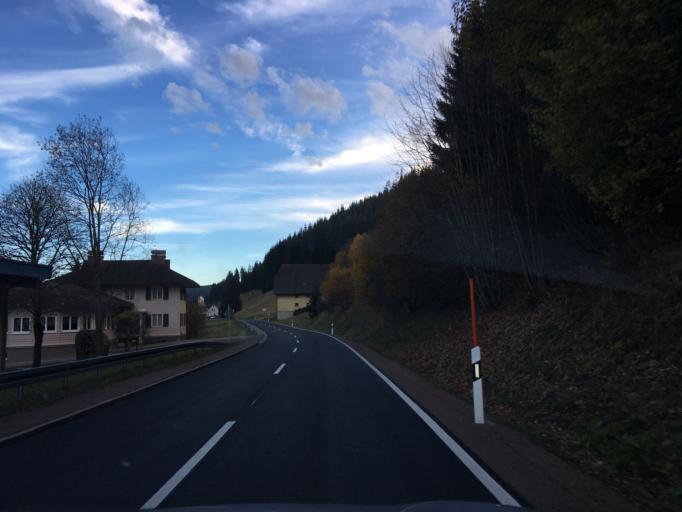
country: DE
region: Baden-Wuerttemberg
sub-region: Freiburg Region
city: Furtwangen im Schwarzwald
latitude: 48.0625
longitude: 8.1959
